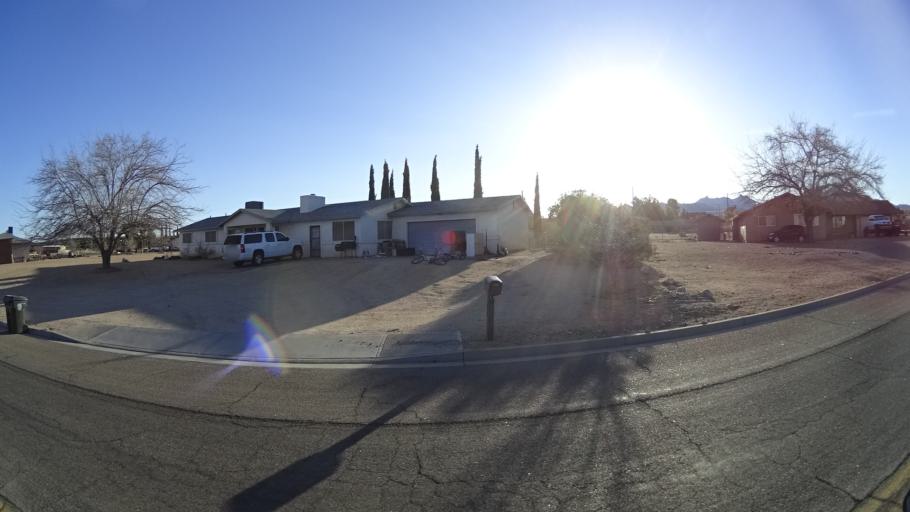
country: US
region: Arizona
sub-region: Mohave County
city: Kingman
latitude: 35.2012
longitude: -114.0114
